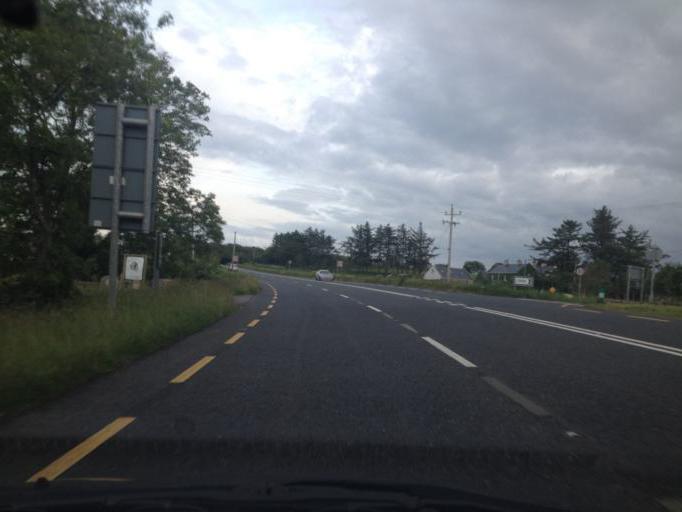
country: IE
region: Connaught
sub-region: Sligo
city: Strandhill
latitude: 54.3856
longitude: -8.5310
